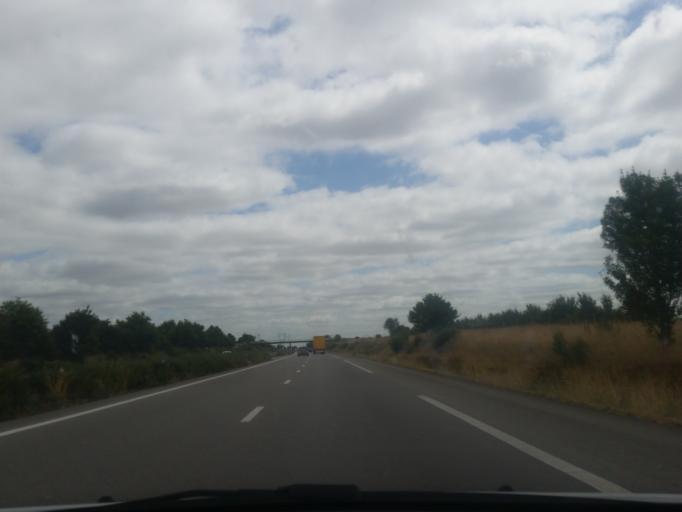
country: FR
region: Pays de la Loire
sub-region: Departement de la Loire-Atlantique
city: Saint-Herblon
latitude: 47.4205
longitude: -1.0675
